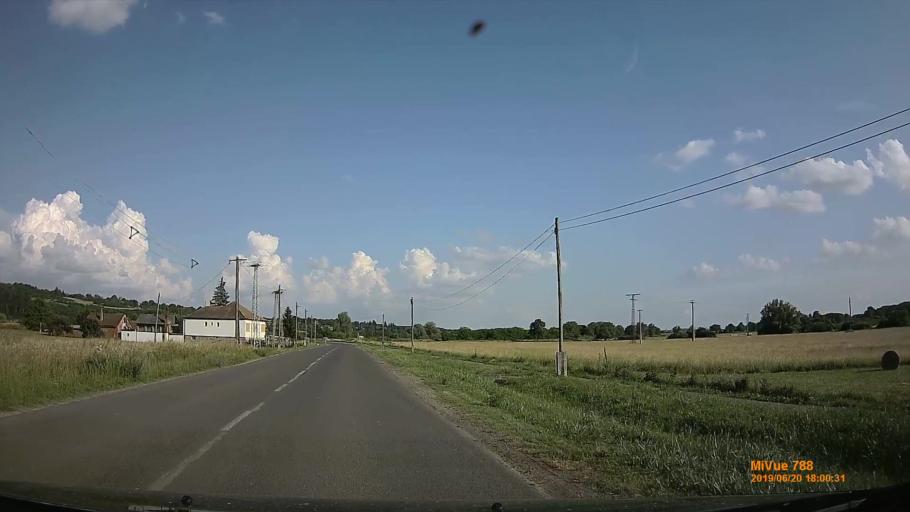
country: HU
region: Baranya
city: Buekkoesd
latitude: 46.0884
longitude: 17.9816
